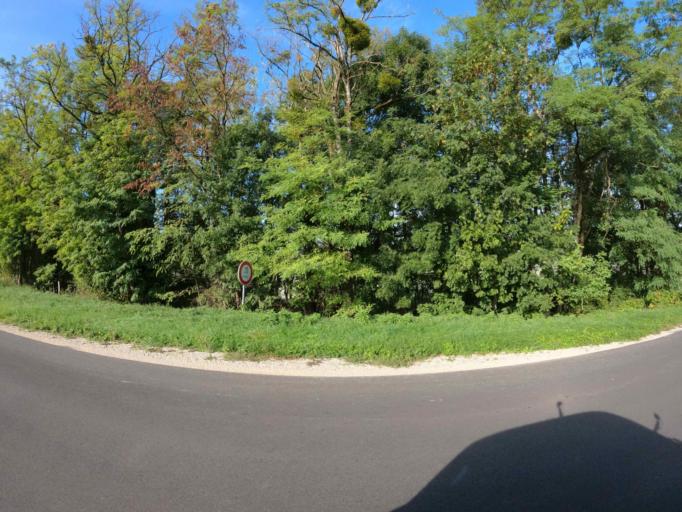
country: FR
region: Franche-Comte
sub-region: Departement du Jura
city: Bletterans
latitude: 46.7340
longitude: 5.5031
